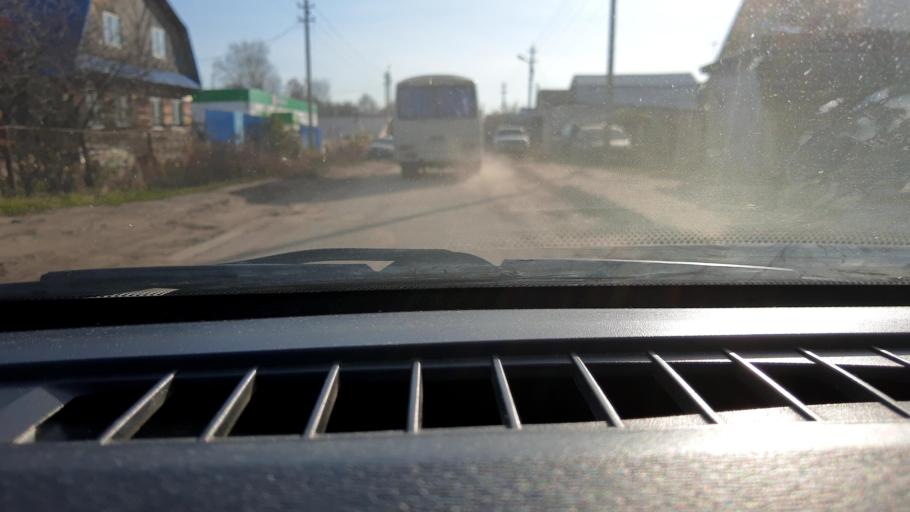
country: RU
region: Nizjnij Novgorod
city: Neklyudovo
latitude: 56.4090
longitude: 43.9803
